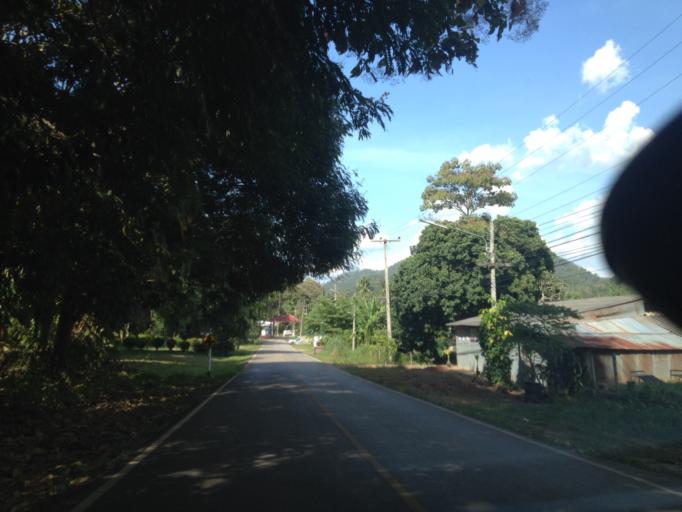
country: TH
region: Chiang Mai
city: Samoeng
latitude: 18.8621
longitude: 98.7238
